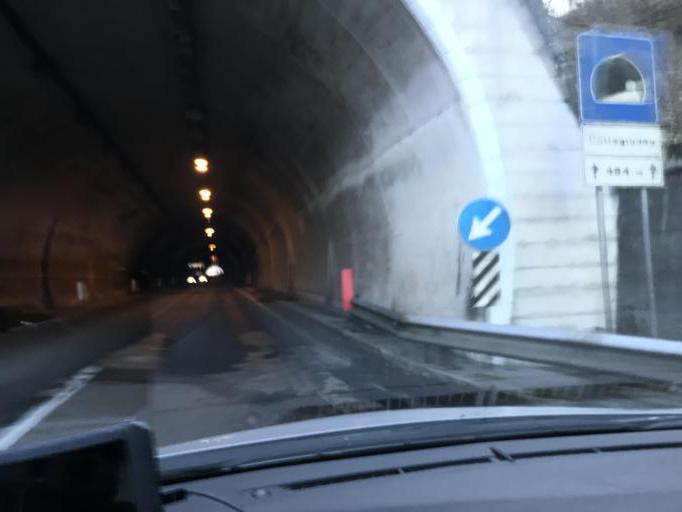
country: IT
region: Latium
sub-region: Provincia di Rieti
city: Fiamignano
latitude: 42.2538
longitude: 13.1504
